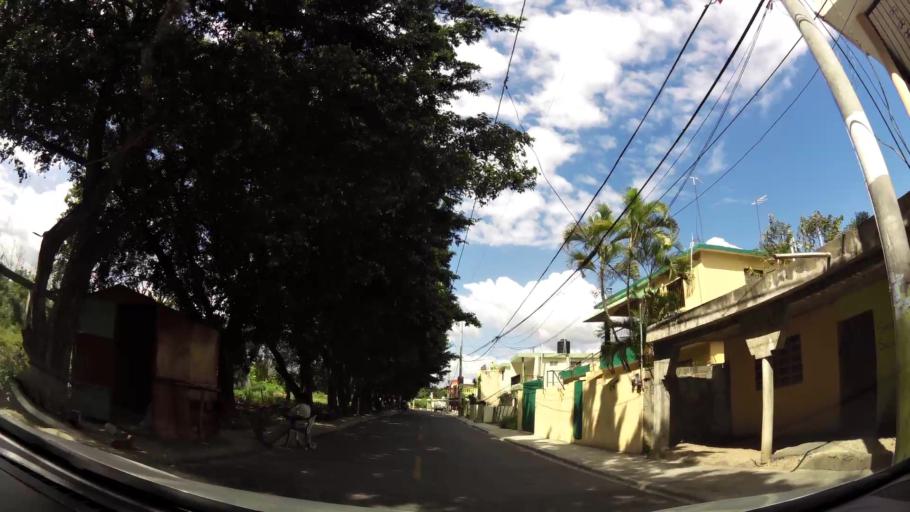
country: DO
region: San Cristobal
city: San Cristobal
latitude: 18.4210
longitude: -70.0945
